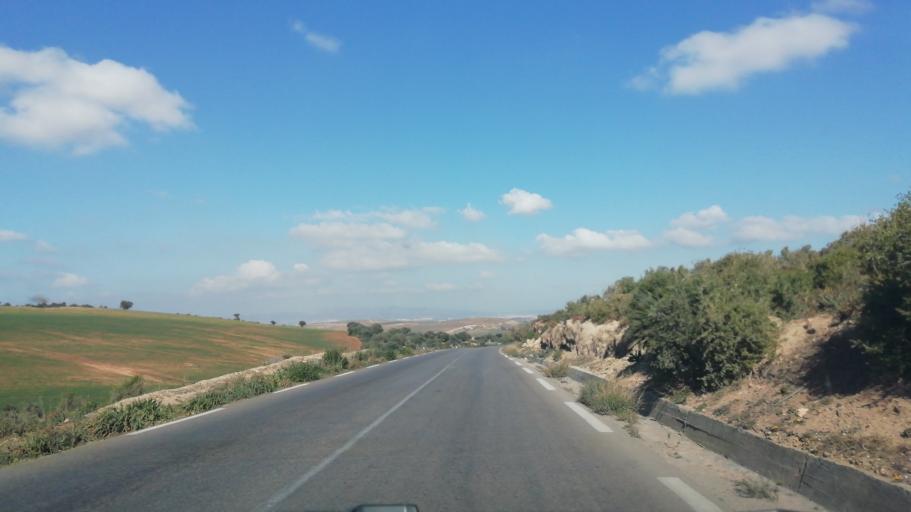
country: DZ
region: Oran
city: Ain el Bya
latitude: 35.7238
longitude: -0.2446
